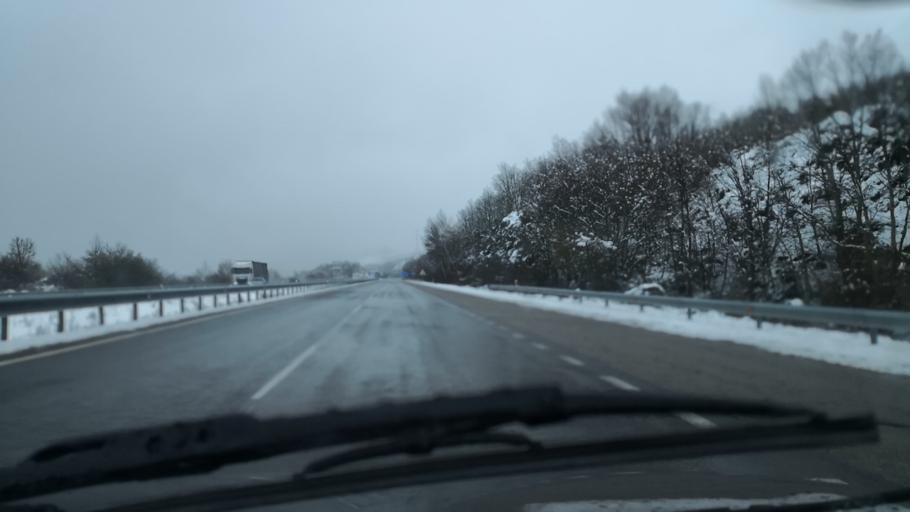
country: ES
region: Castille and Leon
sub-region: Provincia de Zamora
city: Lubian
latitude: 42.0291
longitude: -6.9097
